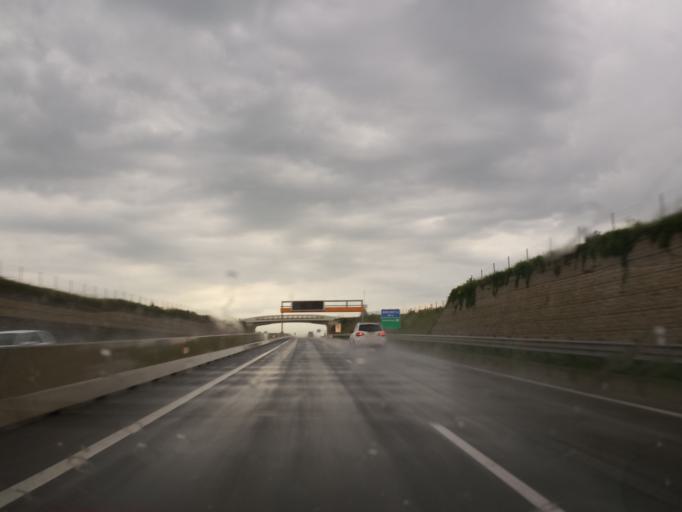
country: AT
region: Lower Austria
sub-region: Politischer Bezirk Mistelbach
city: Wolkersdorf im Weinviertel
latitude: 48.3813
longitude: 16.4906
